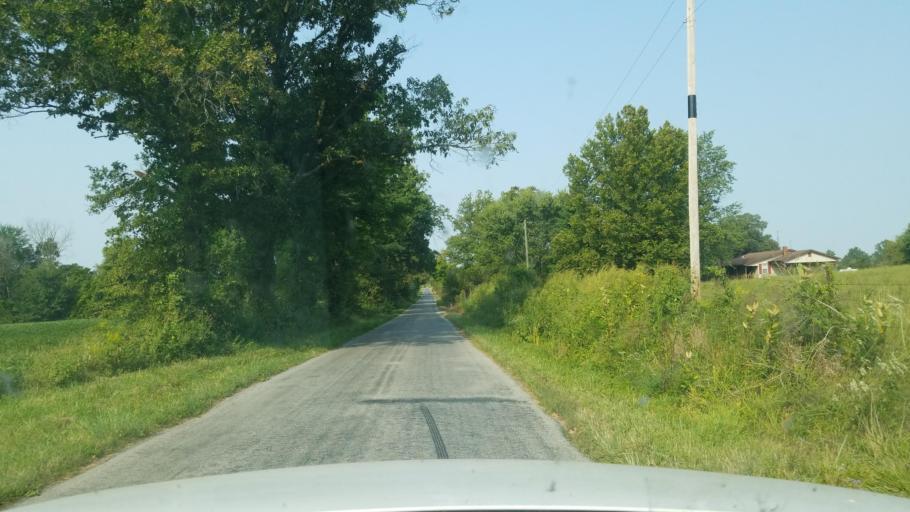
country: US
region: Illinois
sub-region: Saline County
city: Carrier Mills
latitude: 37.7941
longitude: -88.6528
